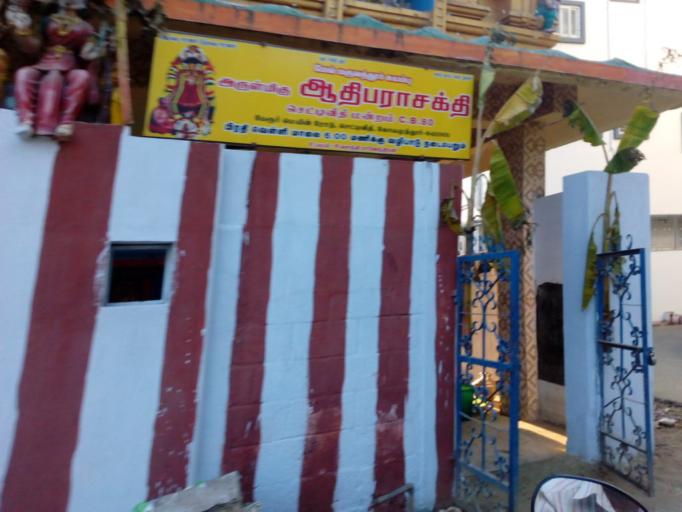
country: IN
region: Tamil Nadu
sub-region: Coimbatore
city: Coimbatore
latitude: 10.9915
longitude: 76.9498
